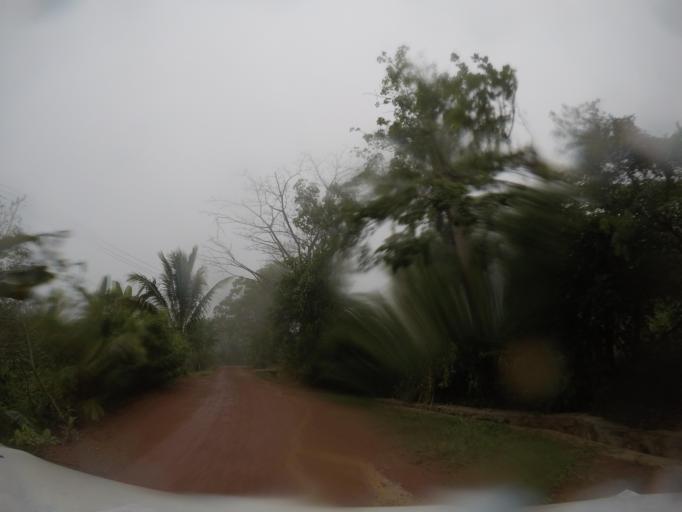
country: TL
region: Baucau
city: Venilale
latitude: -8.6338
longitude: 126.4207
